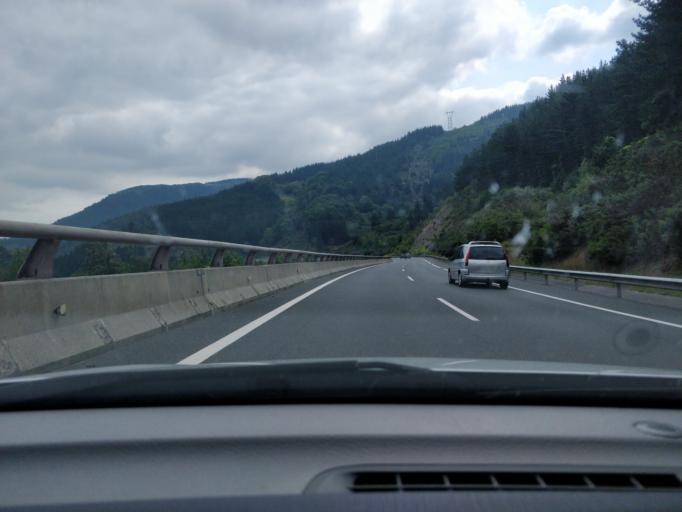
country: ES
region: Basque Country
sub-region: Bizkaia
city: Alonsotegi
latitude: 43.2150
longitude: -3.0320
